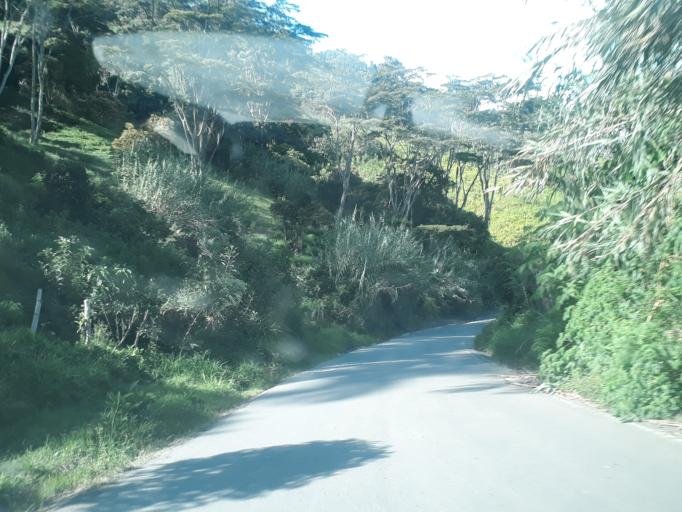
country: CO
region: Santander
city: Velez
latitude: 6.0325
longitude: -73.6550
